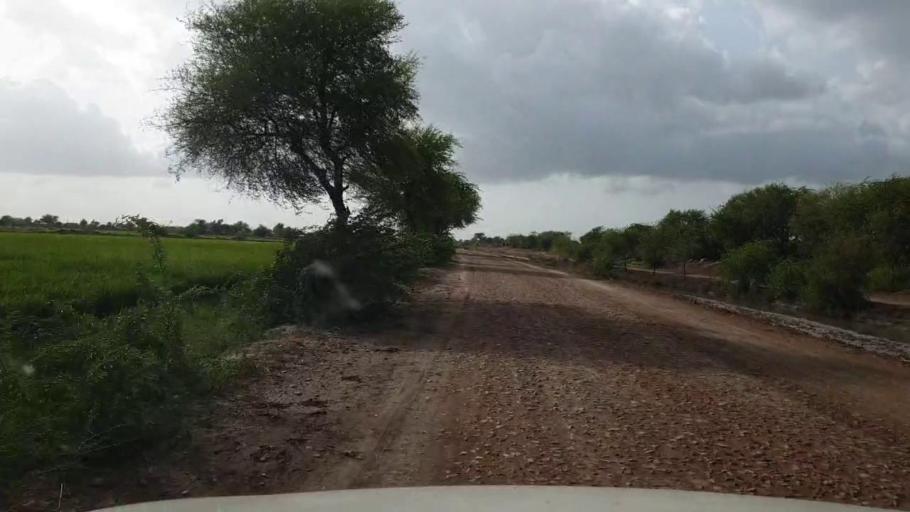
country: PK
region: Sindh
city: Kario
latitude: 24.7869
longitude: 68.5836
